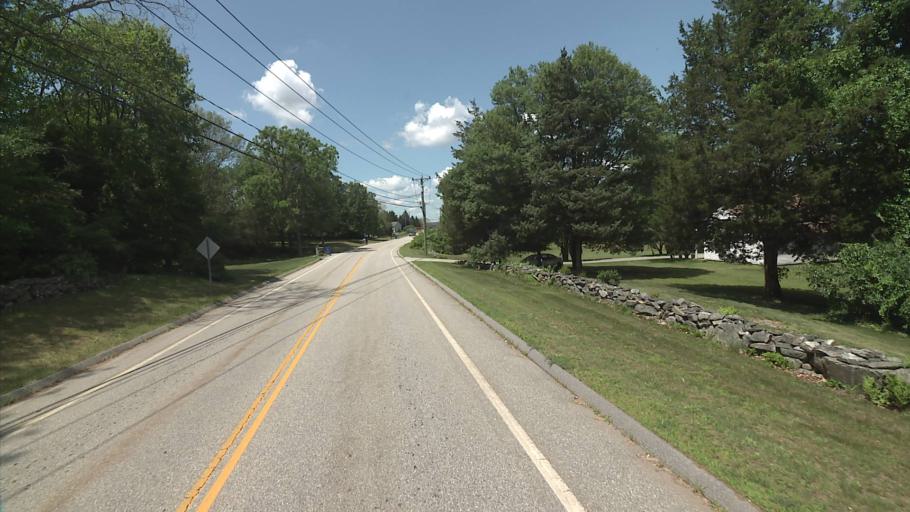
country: US
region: Connecticut
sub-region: New London County
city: Jewett City
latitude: 41.6142
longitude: -71.9524
